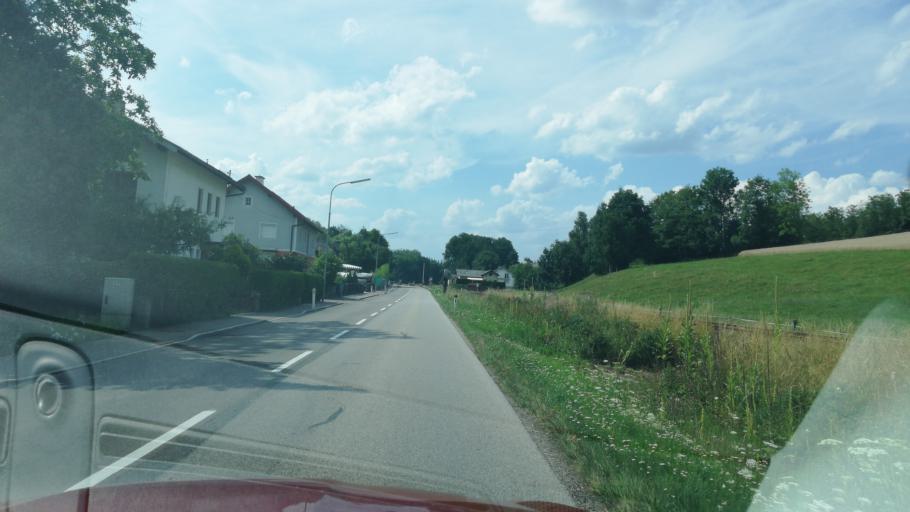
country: AT
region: Upper Austria
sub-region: Politischer Bezirk Vocklabruck
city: Puhret
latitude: 48.0222
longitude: 13.7117
